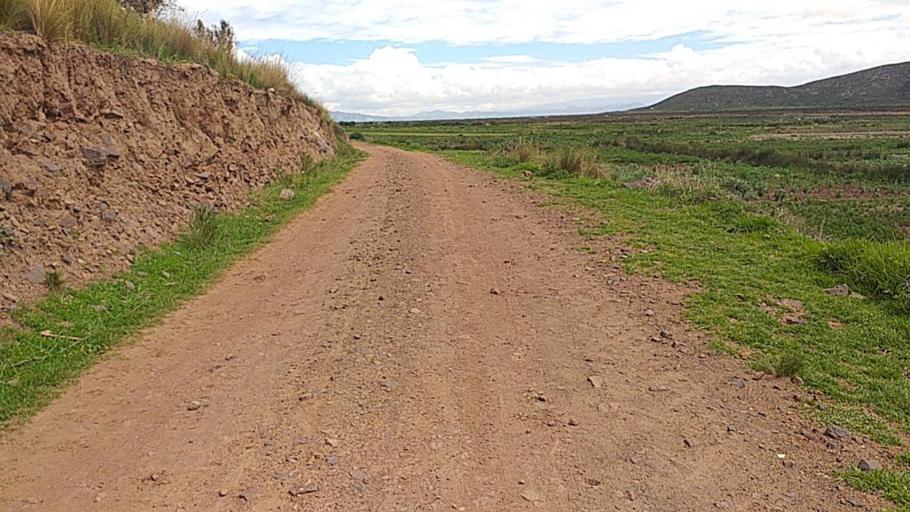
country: BO
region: La Paz
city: Batallas
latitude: -16.3438
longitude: -68.6348
